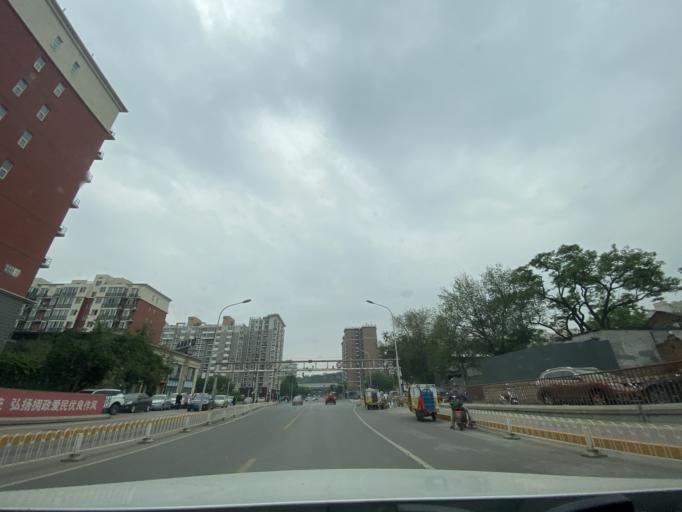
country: CN
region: Beijing
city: Babaoshan
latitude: 39.9293
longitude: 116.2422
